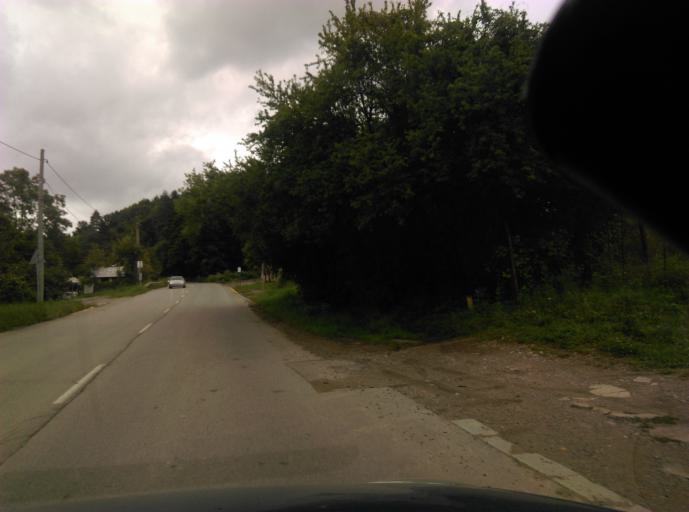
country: BG
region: Sofia-Capital
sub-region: Stolichna Obshtina
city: Sofia
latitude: 42.6096
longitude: 23.3419
